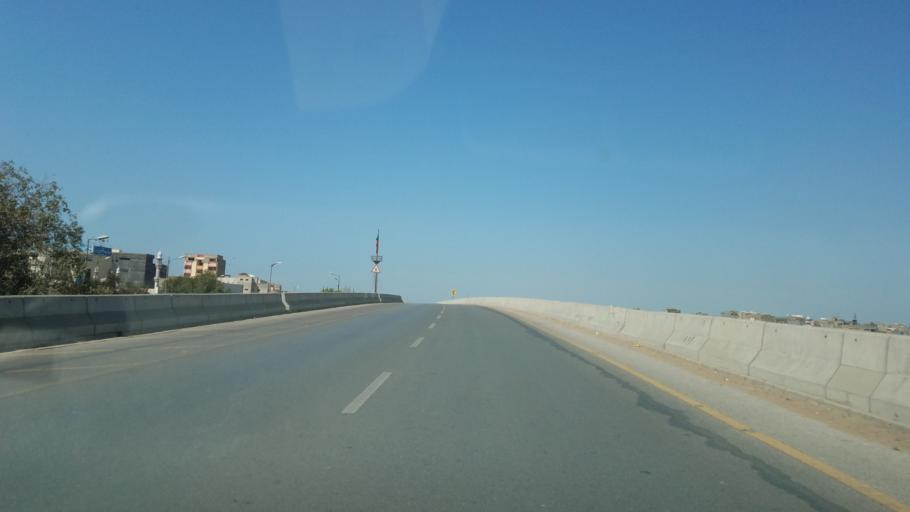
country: PK
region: Sindh
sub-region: Karachi District
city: Karachi
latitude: 24.8802
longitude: 66.9969
